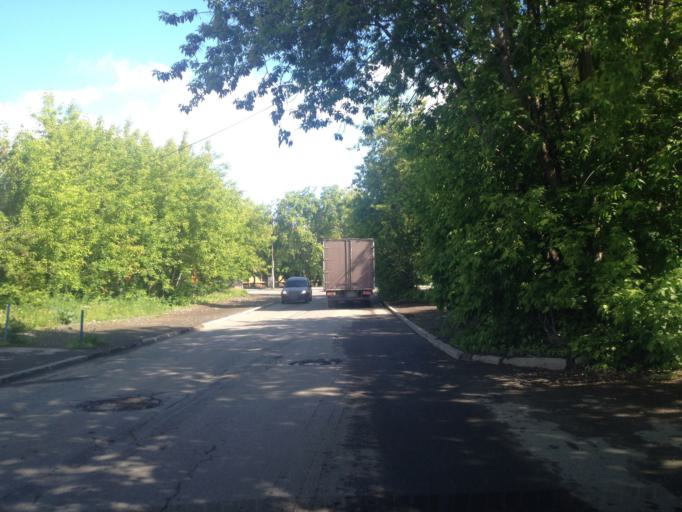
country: RU
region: Sverdlovsk
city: Sovkhoznyy
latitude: 56.7665
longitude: 60.6230
